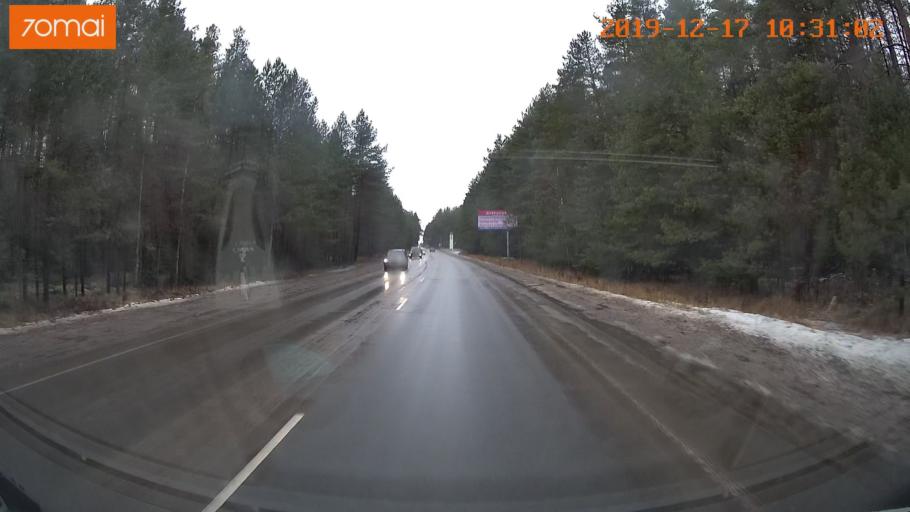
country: RU
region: Vladimir
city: Gus'-Khrustal'nyy
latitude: 55.6383
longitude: 40.7015
